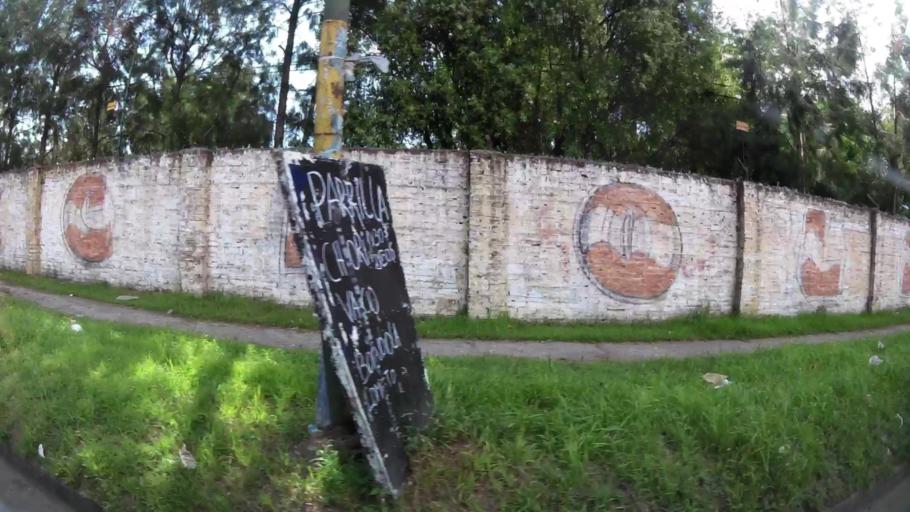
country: AR
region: Buenos Aires
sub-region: Partido de Merlo
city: Merlo
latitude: -34.6411
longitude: -58.7163
